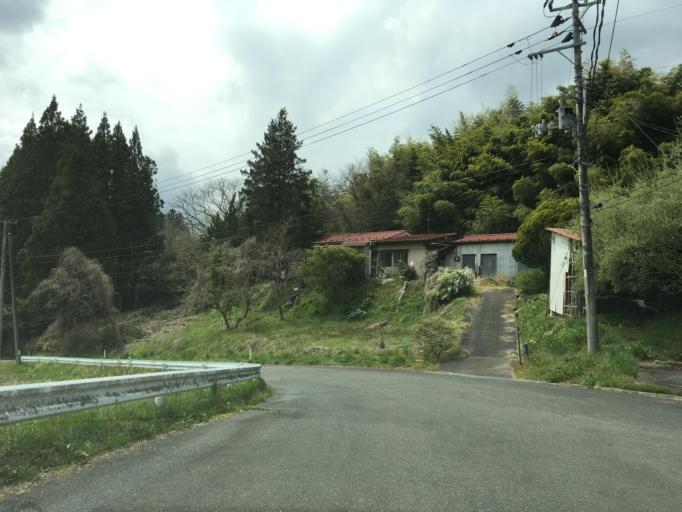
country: JP
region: Iwate
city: Ichinoseki
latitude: 38.8566
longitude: 141.3175
